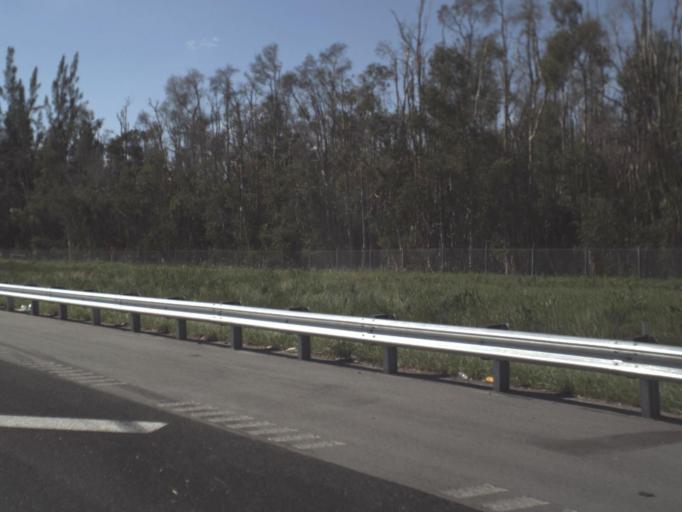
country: US
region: Florida
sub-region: Miami-Dade County
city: Doral
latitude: 25.8653
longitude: -80.3880
